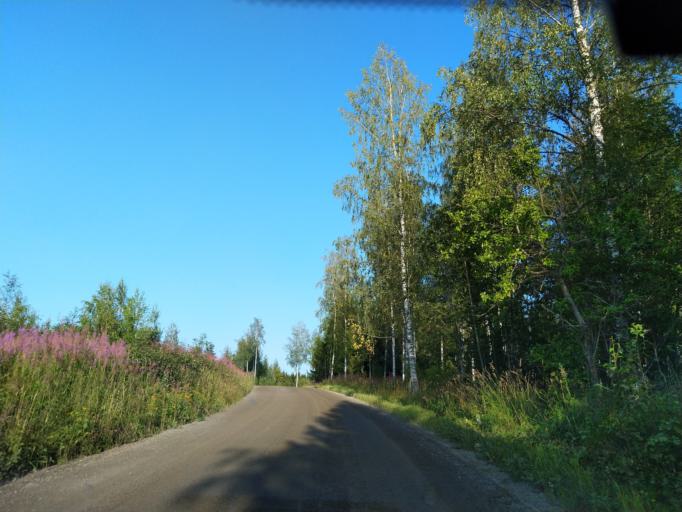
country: FI
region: Central Finland
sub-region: Jaemsae
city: Kuhmoinen
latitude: 61.6041
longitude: 25.1395
